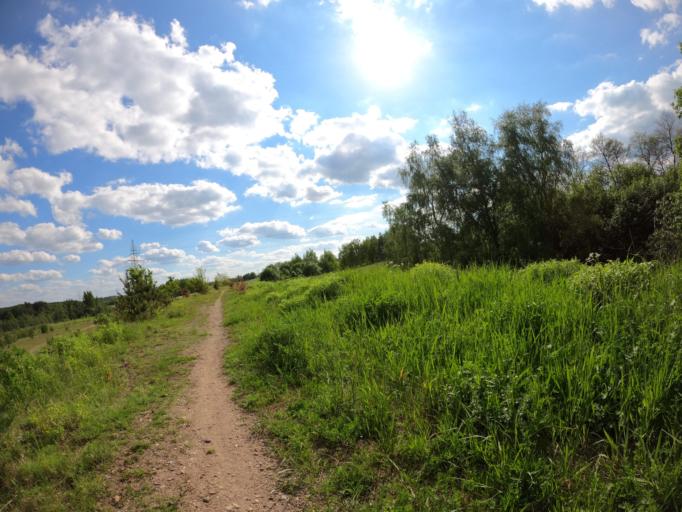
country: PL
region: Warmian-Masurian Voivodeship
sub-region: Powiat lidzbarski
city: Lidzbark Warminski
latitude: 54.1431
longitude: 20.6065
